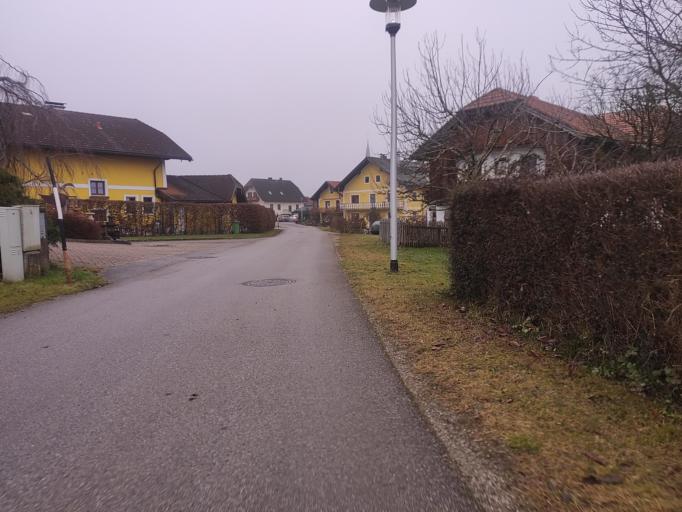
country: AT
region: Salzburg
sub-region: Politischer Bezirk Salzburg-Umgebung
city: Schleedorf
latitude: 47.9522
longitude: 13.1552
